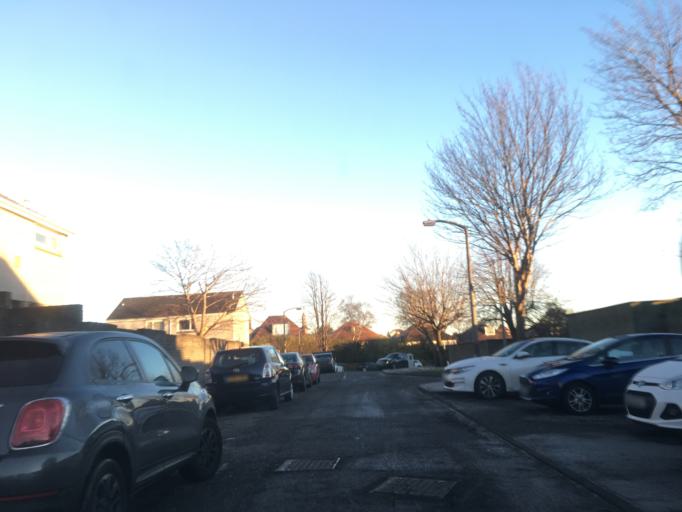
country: GB
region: Scotland
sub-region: Edinburgh
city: Currie
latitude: 55.9472
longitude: -3.3028
